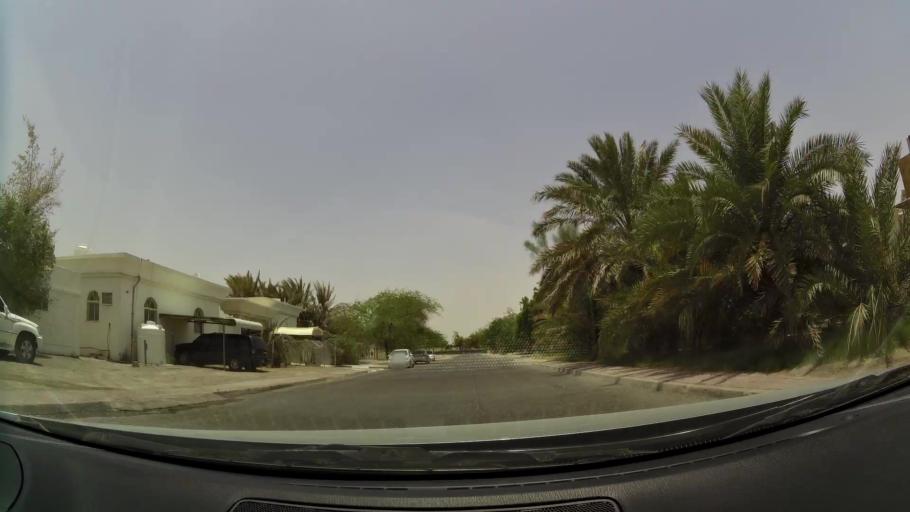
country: AE
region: Abu Dhabi
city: Al Ain
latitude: 24.2131
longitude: 55.7352
